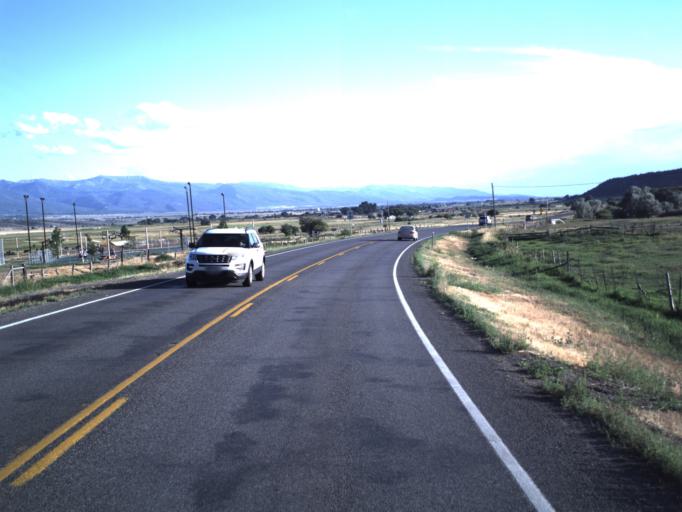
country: US
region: Utah
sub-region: Sanpete County
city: Fairview
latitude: 39.6215
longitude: -111.4394
